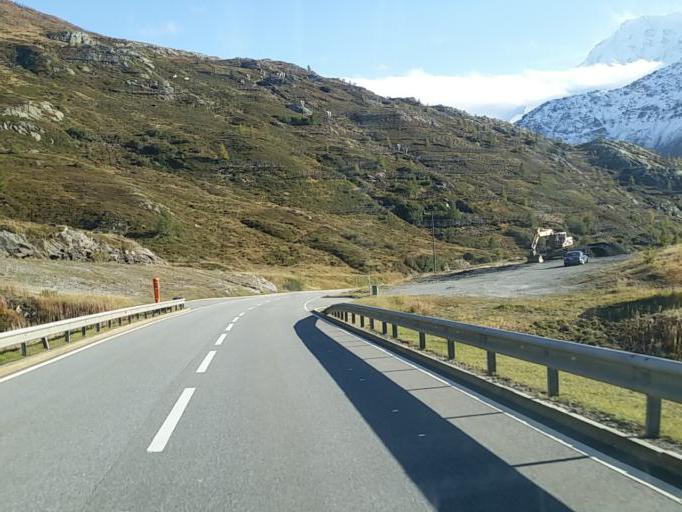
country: CH
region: Valais
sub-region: Brig District
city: Brig
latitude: 46.2410
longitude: 8.0211
